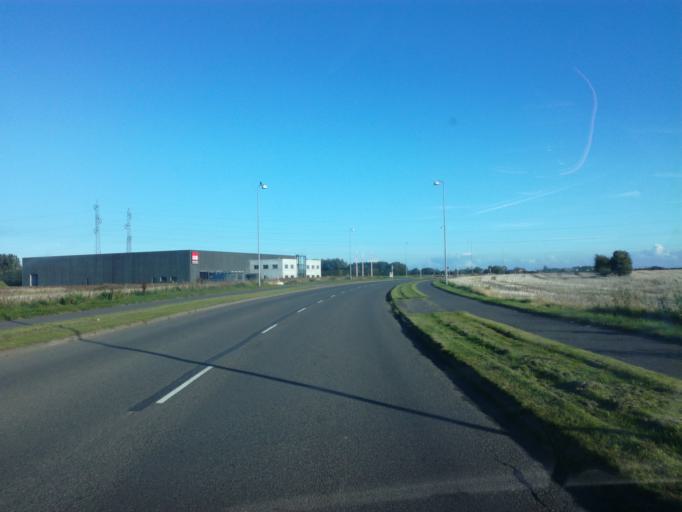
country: DK
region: South Denmark
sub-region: Fredericia Kommune
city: Taulov
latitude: 55.5553
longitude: 9.6587
